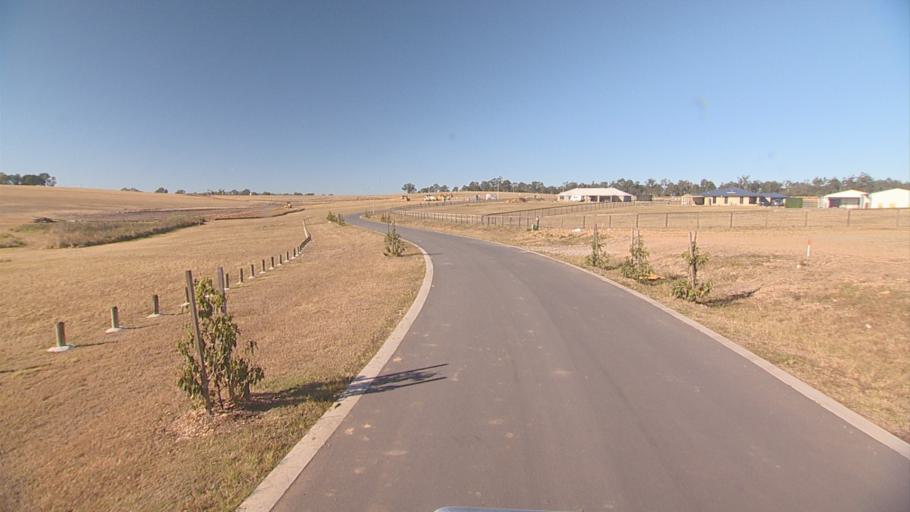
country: AU
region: Queensland
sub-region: Logan
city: North Maclean
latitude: -27.8094
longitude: 152.9950
